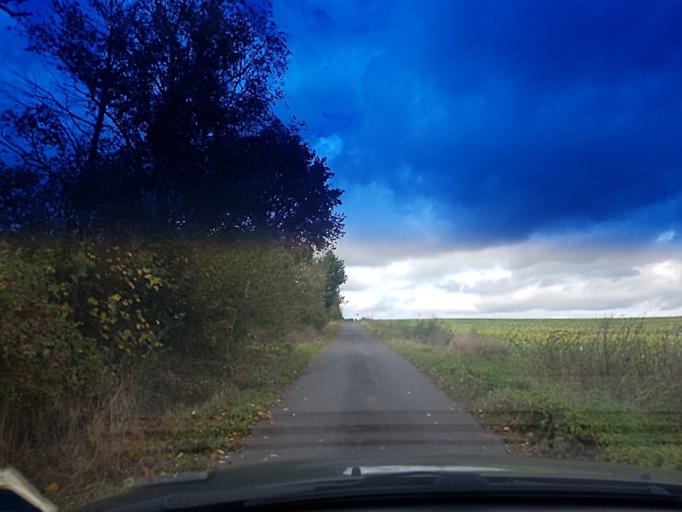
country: DE
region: Bavaria
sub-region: Regierungsbezirk Mittelfranken
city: Wachenroth
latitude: 49.7530
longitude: 10.6803
